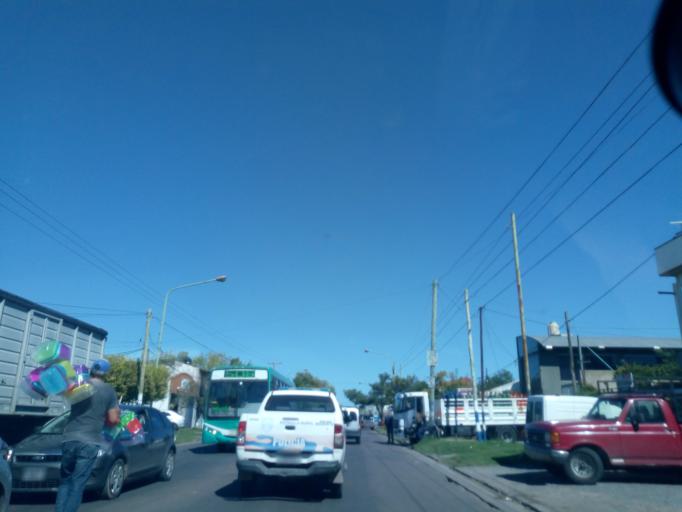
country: AR
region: Buenos Aires
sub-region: Partido de La Plata
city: La Plata
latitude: -34.9604
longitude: -57.9726
